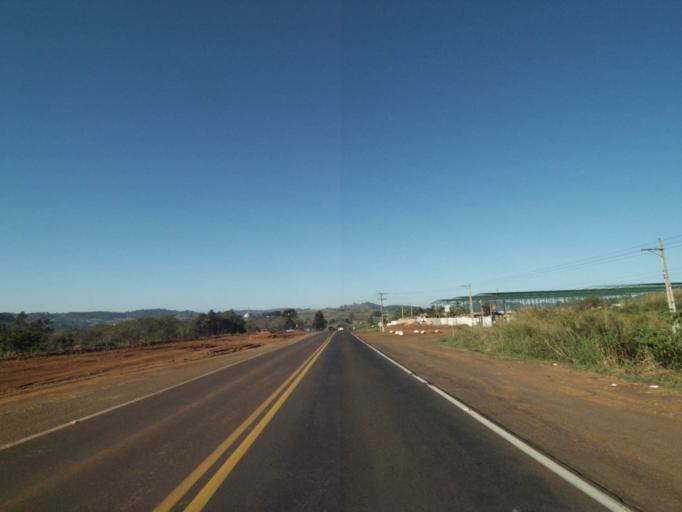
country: BR
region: Parana
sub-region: Londrina
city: Londrina
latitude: -23.3955
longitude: -51.1338
